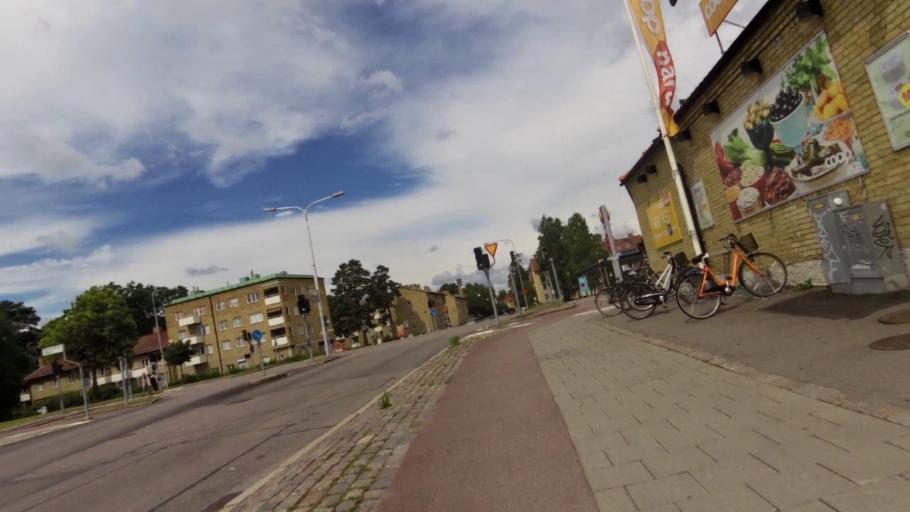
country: SE
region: OEstergoetland
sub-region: Linkopings Kommun
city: Linkoping
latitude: 58.4072
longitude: 15.5975
